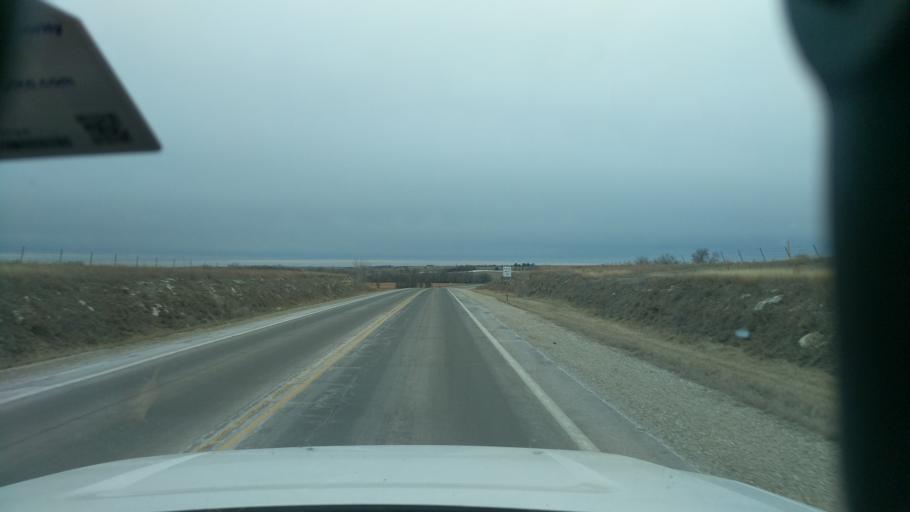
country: US
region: Kansas
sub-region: Dickinson County
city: Herington
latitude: 38.6603
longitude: -96.9327
